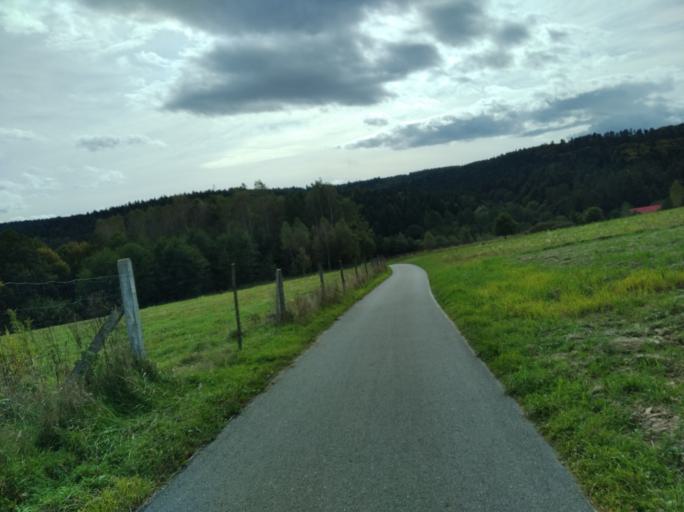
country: PL
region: Subcarpathian Voivodeship
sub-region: Powiat strzyzowski
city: Jawornik
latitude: 49.8356
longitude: 21.8934
